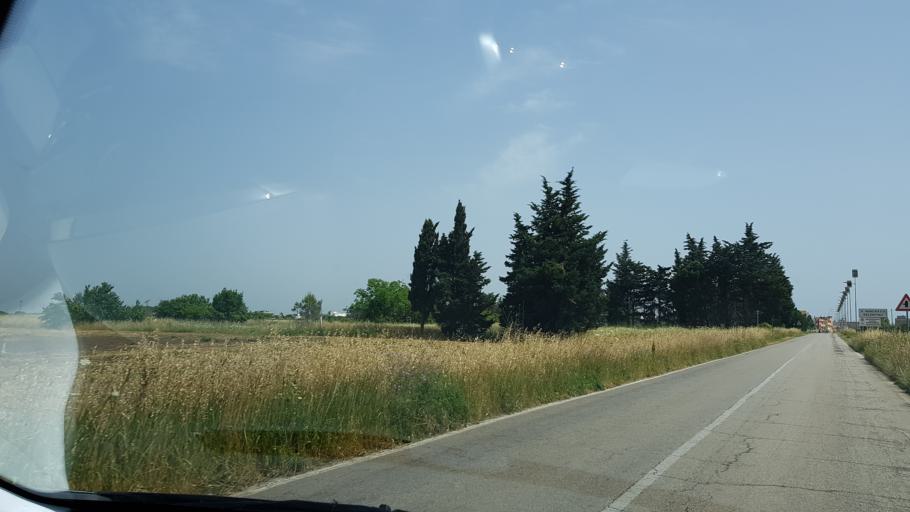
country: IT
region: Apulia
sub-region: Provincia di Brindisi
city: San Pancrazio Salentino
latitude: 40.4288
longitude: 17.8405
